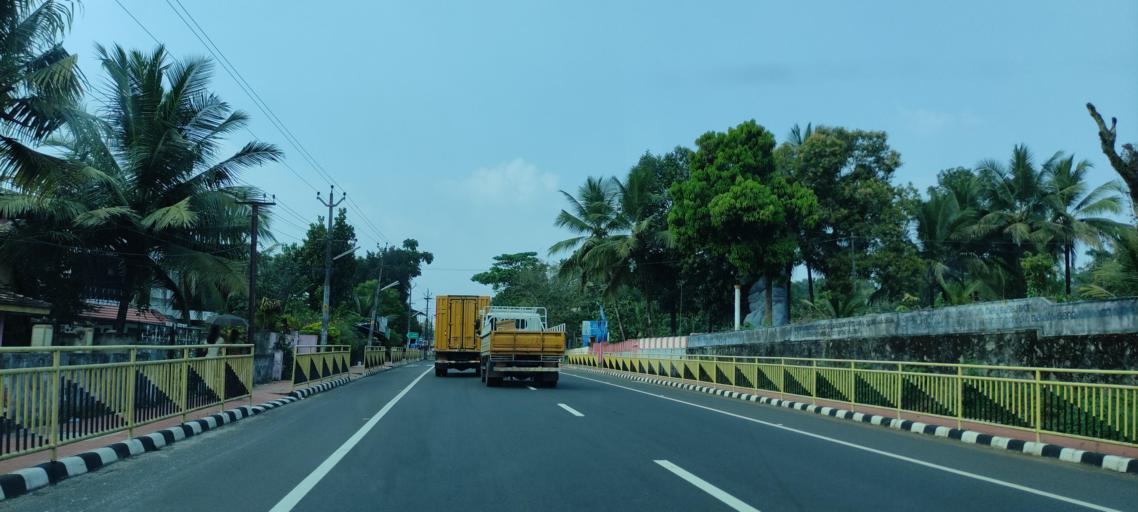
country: IN
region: Kerala
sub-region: Alappuzha
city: Chengannur
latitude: 9.2608
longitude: 76.6572
